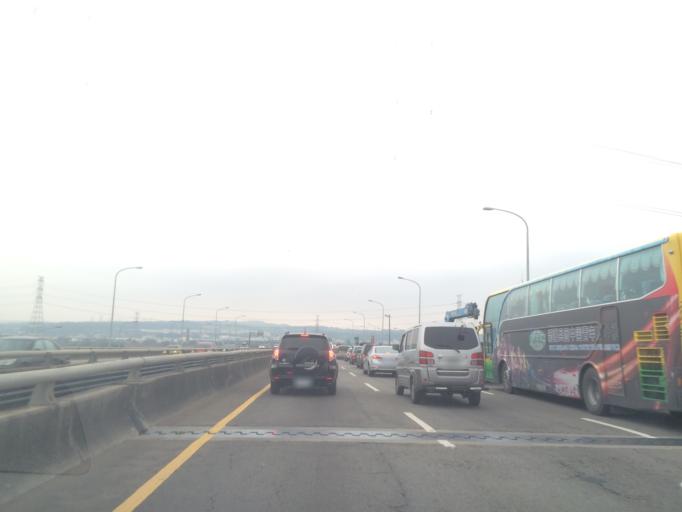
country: TW
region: Taiwan
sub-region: Changhua
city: Chang-hua
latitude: 24.1029
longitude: 120.6128
